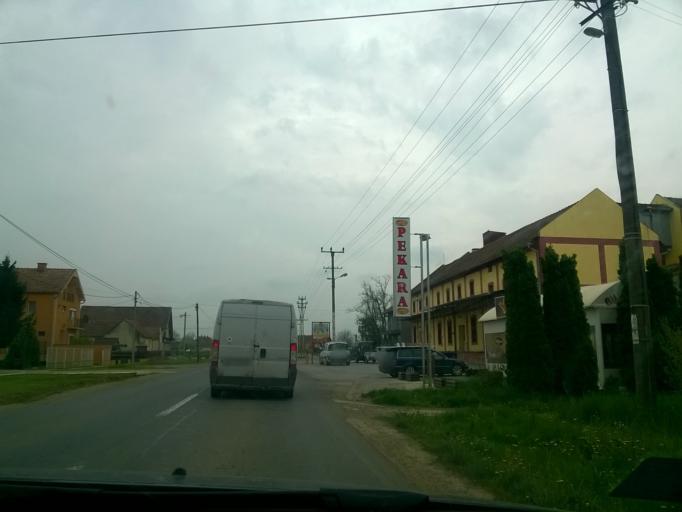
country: RS
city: Platicevo
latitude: 44.8301
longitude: 19.7768
